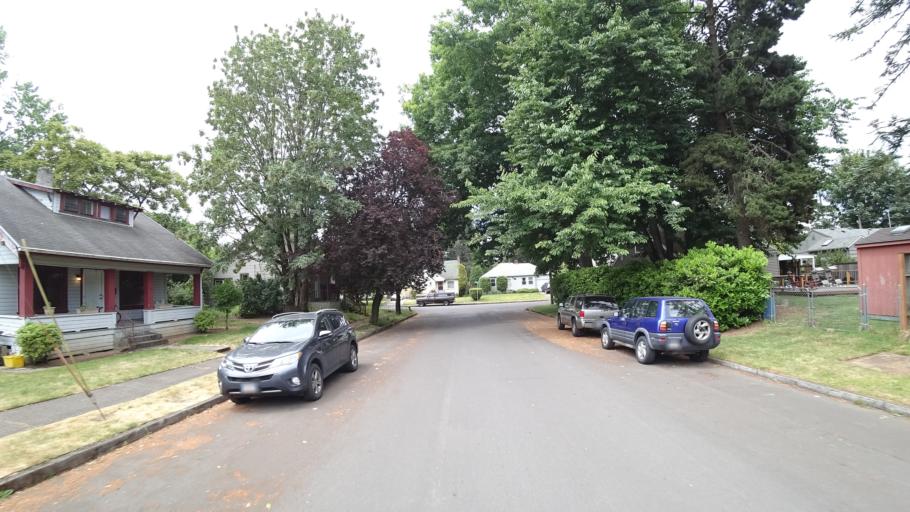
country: US
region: Oregon
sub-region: Washington County
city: West Haven
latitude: 45.5781
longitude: -122.7321
